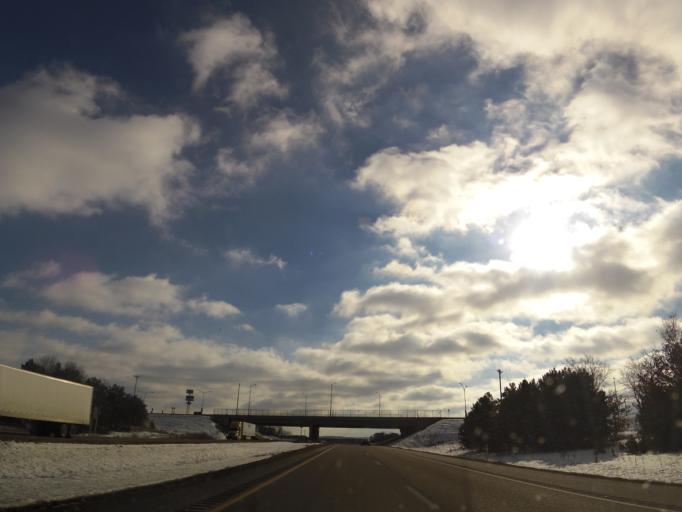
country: US
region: Wisconsin
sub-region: Trempealeau County
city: Osseo
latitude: 44.5806
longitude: -91.2062
